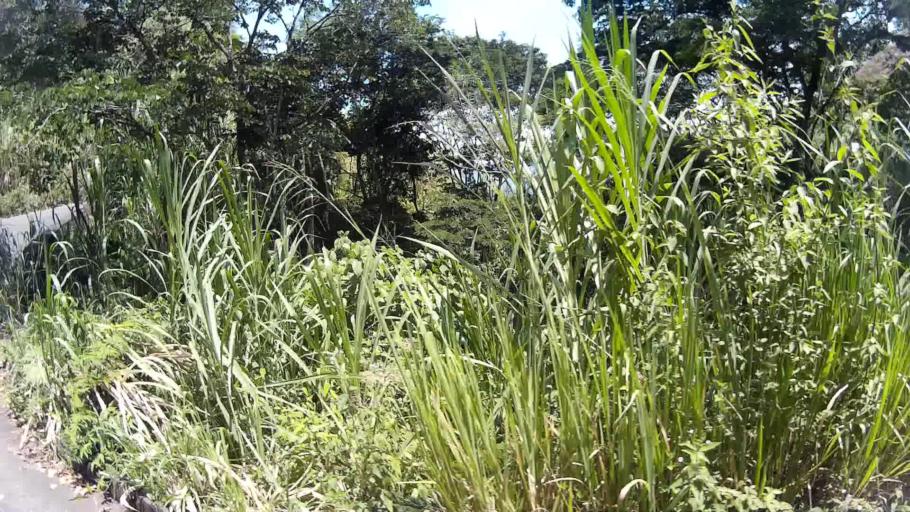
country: CO
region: Risaralda
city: La Virginia
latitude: 4.9413
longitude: -75.8403
